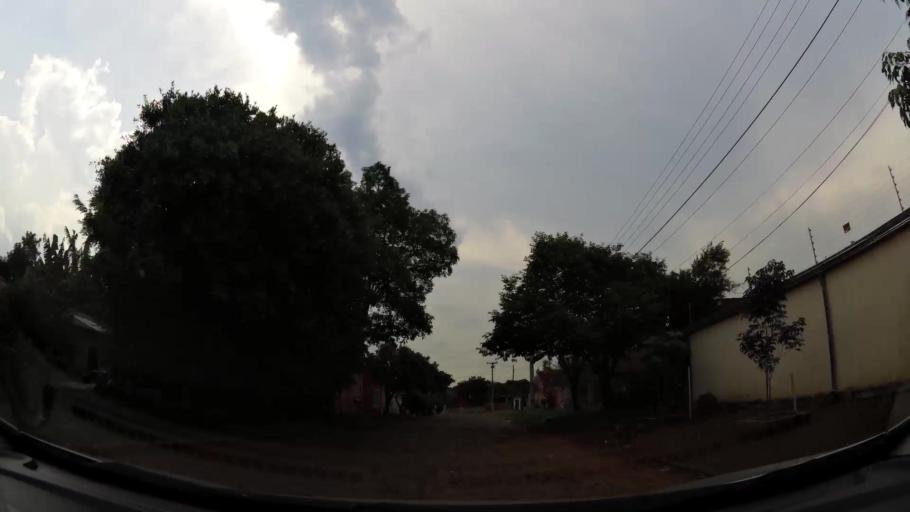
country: PY
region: Alto Parana
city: Presidente Franco
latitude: -25.5429
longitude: -54.6114
